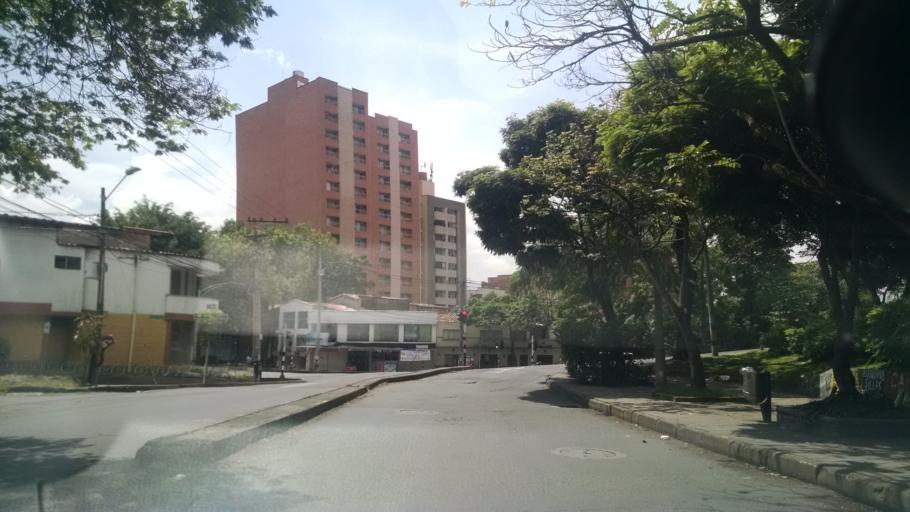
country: CO
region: Antioquia
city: Medellin
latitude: 6.2647
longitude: -75.6005
